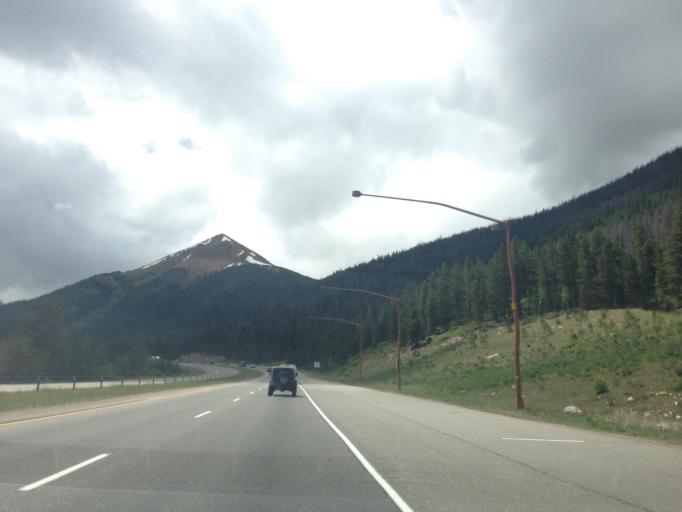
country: US
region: Colorado
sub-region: Clear Creek County
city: Georgetown
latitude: 39.7011
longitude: -105.8402
